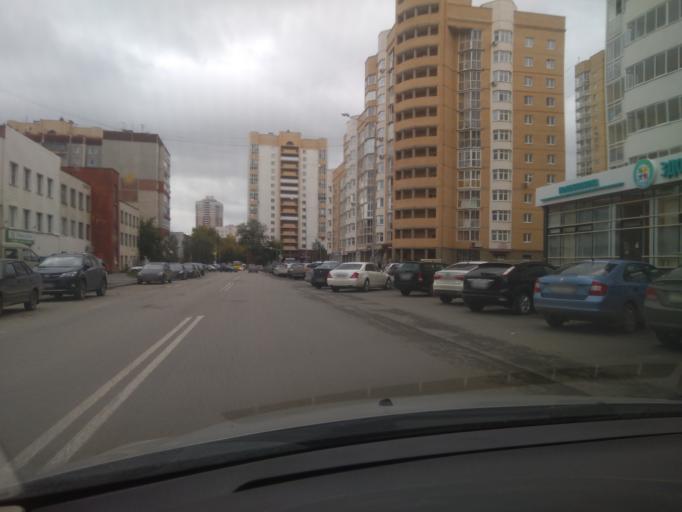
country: RU
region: Sverdlovsk
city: Yekaterinburg
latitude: 56.8047
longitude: 60.6145
